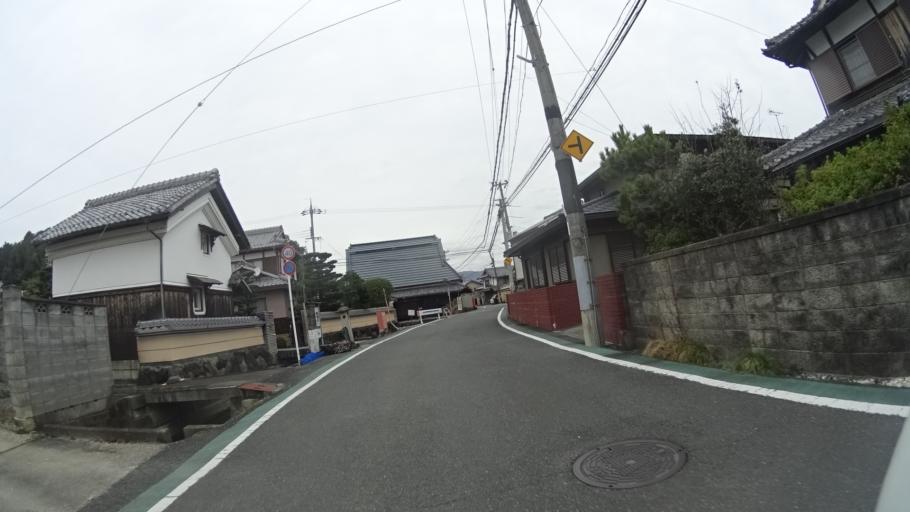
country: JP
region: Kyoto
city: Kameoka
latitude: 35.0539
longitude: 135.5453
